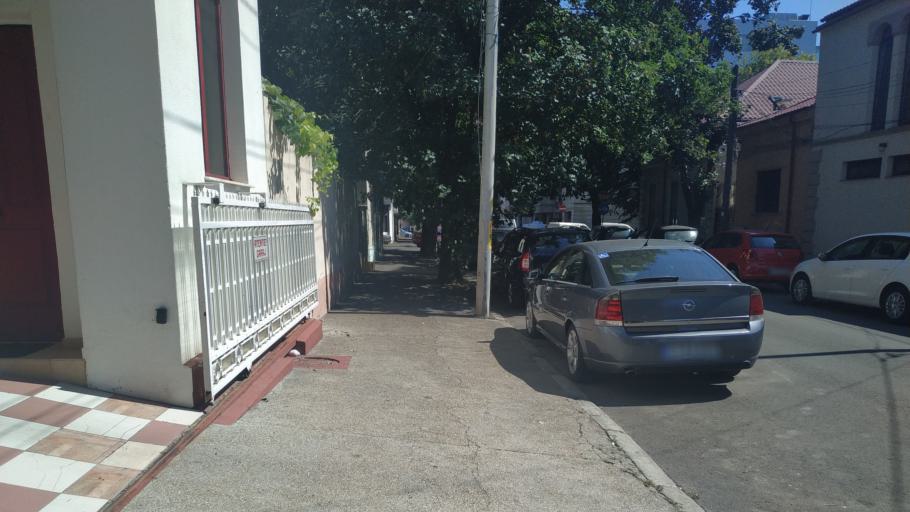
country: RO
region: Constanta
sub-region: Municipiul Constanta
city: Constanta
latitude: 44.1799
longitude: 28.6460
